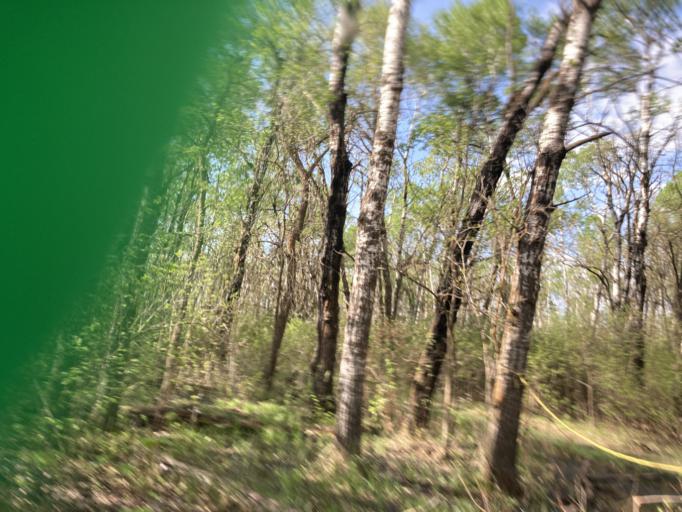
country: CA
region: Manitoba
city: Brandon
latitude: 49.7211
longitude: -99.8957
